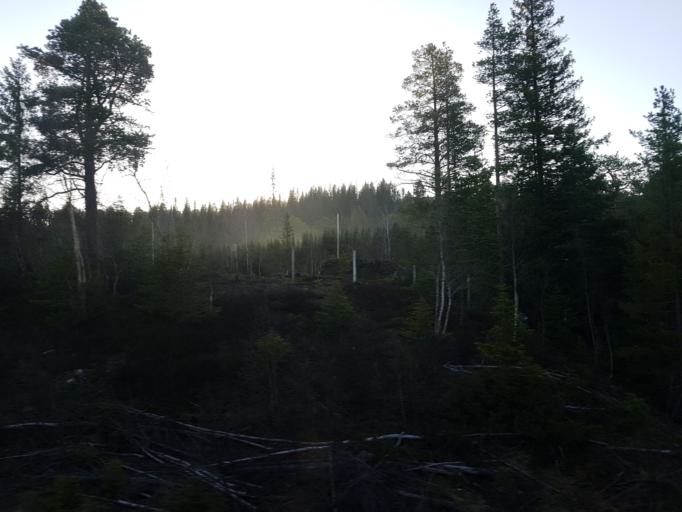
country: NO
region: Sor-Trondelag
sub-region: Rennebu
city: Berkak
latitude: 62.8356
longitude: 10.0216
